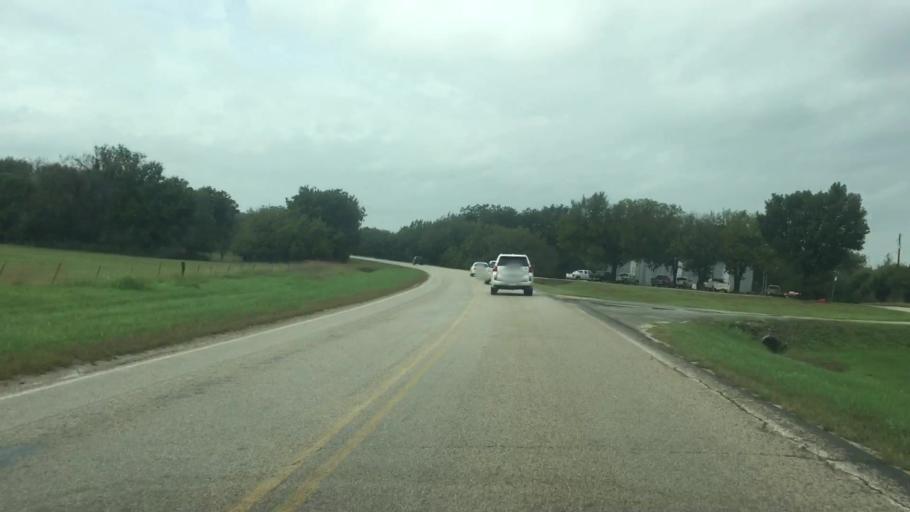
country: US
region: Kansas
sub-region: Allen County
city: Iola
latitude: 37.8854
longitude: -95.4293
